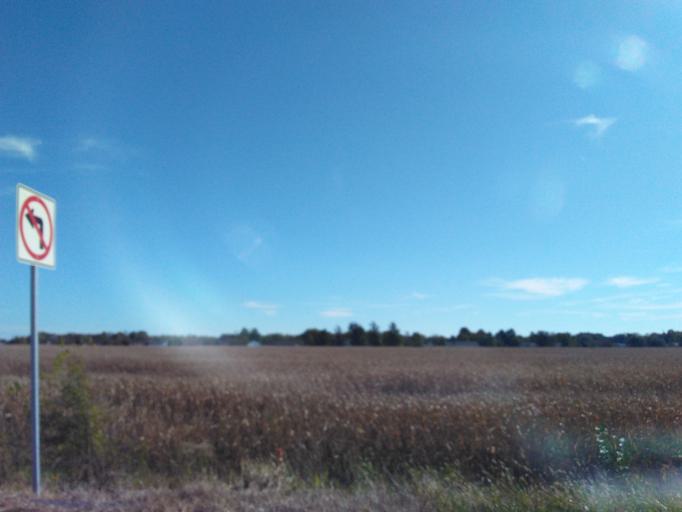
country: US
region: Illinois
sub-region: Madison County
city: Highland
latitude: 38.7837
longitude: -89.6310
